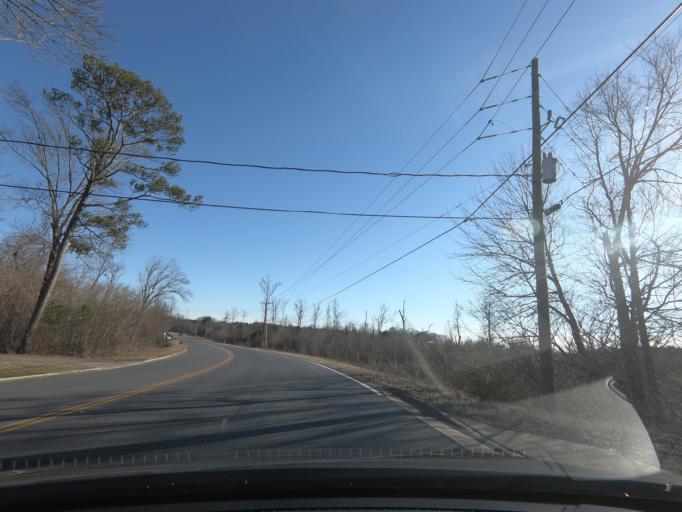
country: US
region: Georgia
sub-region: Gordon County
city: Calhoun
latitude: 34.4567
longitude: -84.9166
